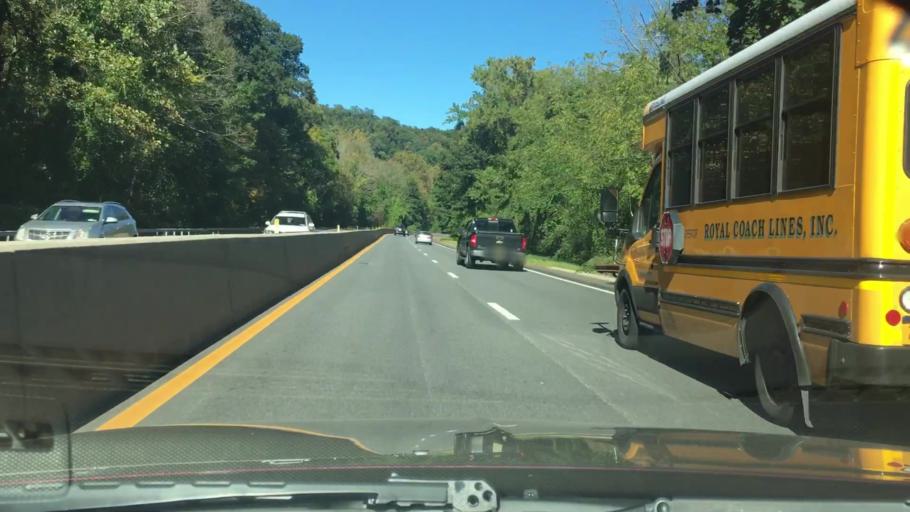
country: US
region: New York
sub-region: Westchester County
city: Pleasantville
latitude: 41.1385
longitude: -73.7927
